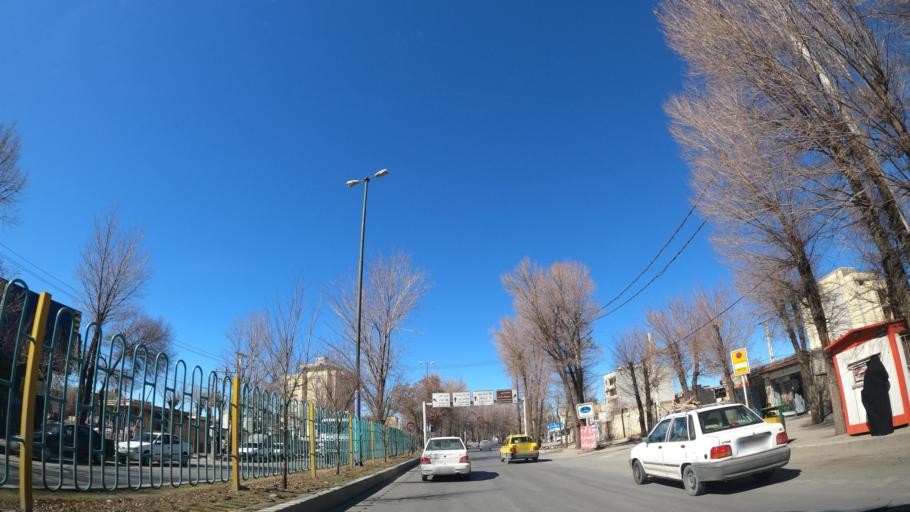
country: IR
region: Chahar Mahall va Bakhtiari
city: Shahrekord
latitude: 32.3111
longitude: 50.8868
